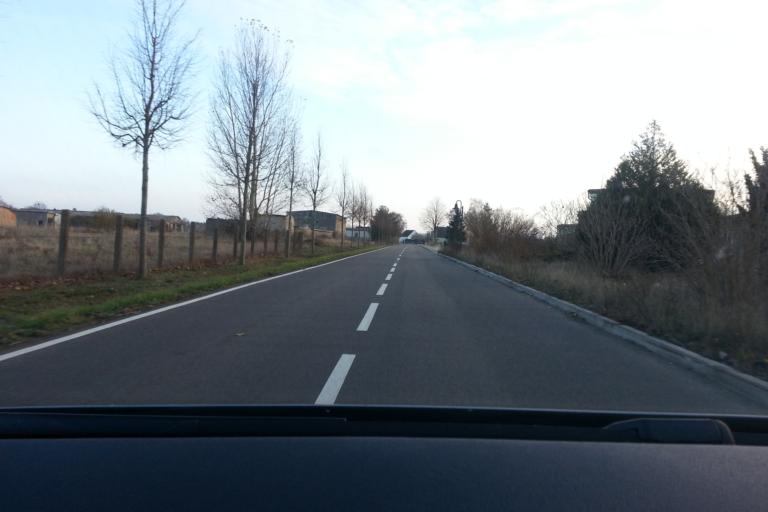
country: DE
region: Mecklenburg-Vorpommern
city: Strasburg
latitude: 53.6193
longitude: 13.7664
